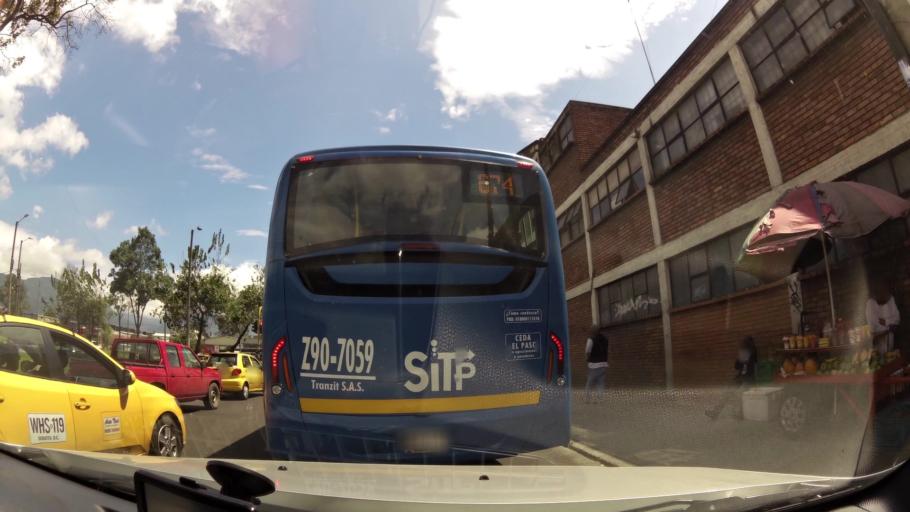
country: CO
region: Bogota D.C.
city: Bogota
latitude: 4.6269
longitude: -74.0959
